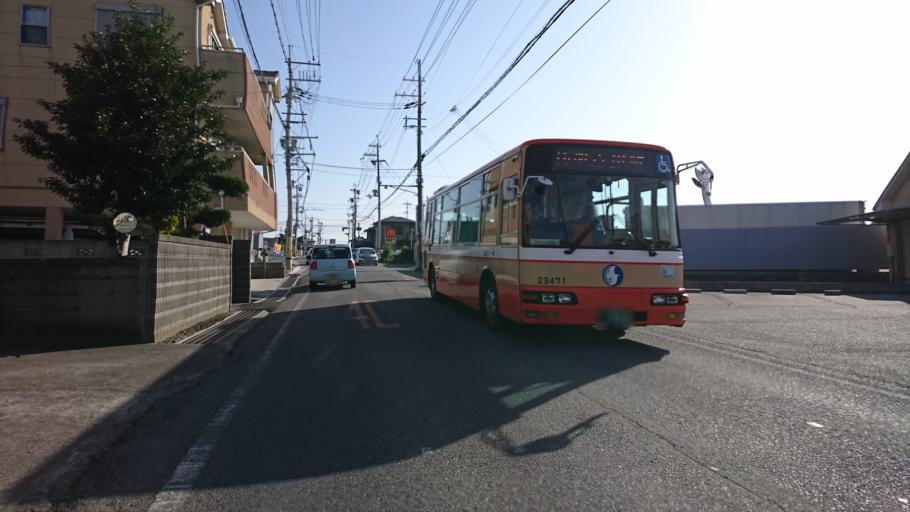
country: JP
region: Hyogo
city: Kakogawacho-honmachi
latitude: 34.7639
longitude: 134.8739
